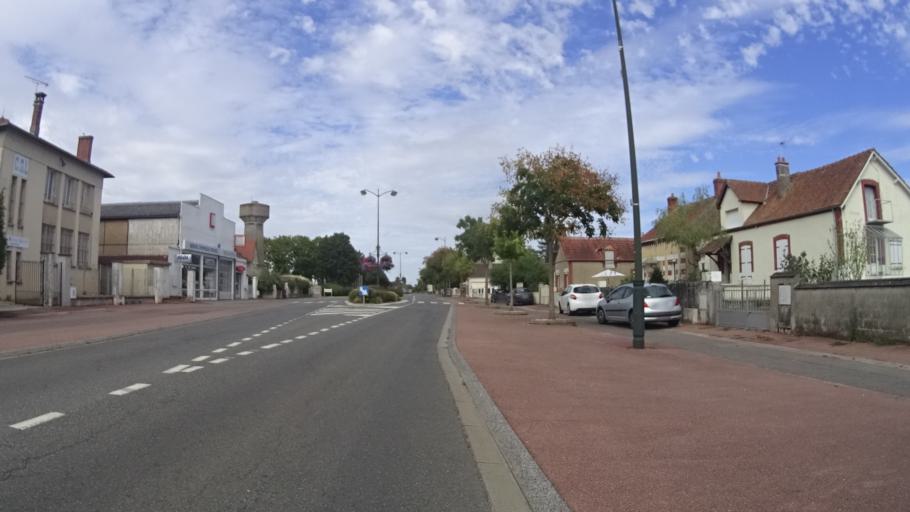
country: FR
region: Centre
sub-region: Departement du Loiret
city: Briare
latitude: 47.6489
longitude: 2.7357
